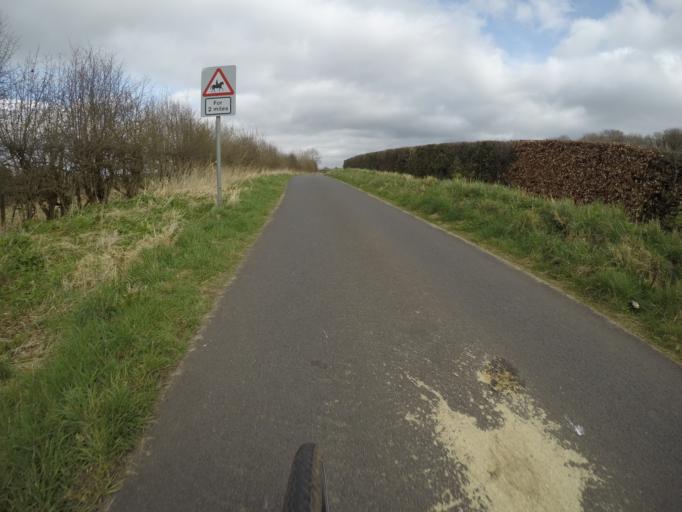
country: GB
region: Scotland
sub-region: North Ayrshire
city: Irvine
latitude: 55.6363
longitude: -4.6322
